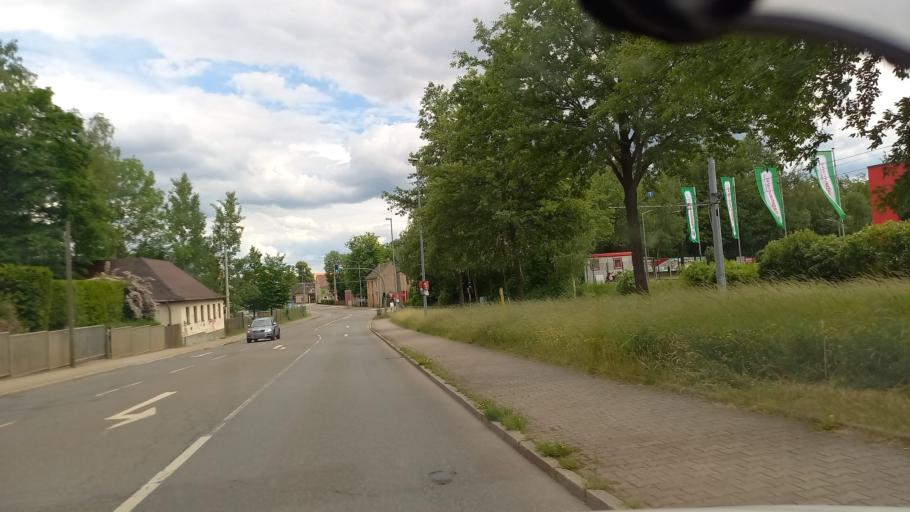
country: DE
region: Saxony
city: Weissenborn
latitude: 50.7212
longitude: 12.4485
